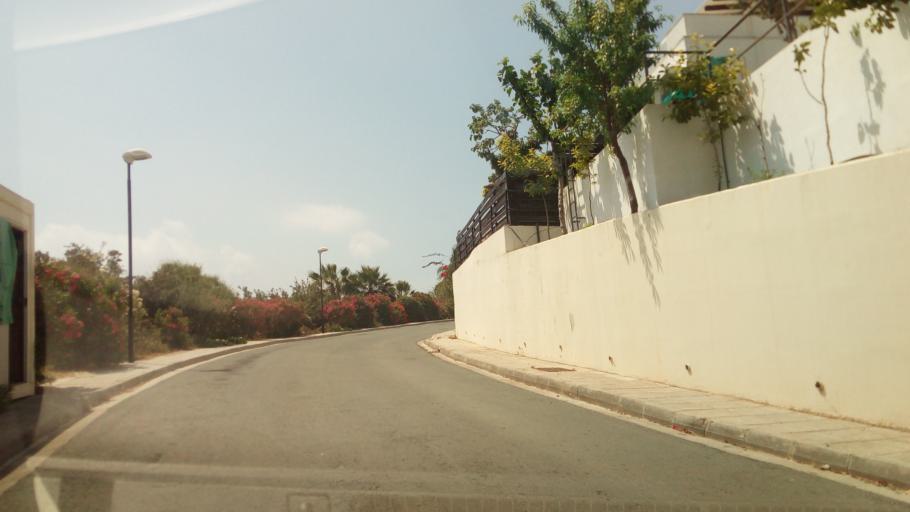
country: CY
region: Limassol
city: Pissouri
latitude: 34.6534
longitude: 32.7265
